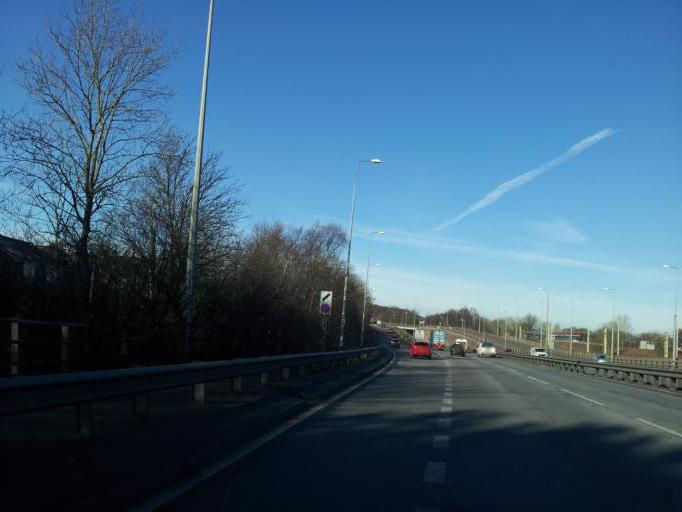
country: GB
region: England
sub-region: Stoke-on-Trent
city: Stoke-on-Trent
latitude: 53.0377
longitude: -2.2119
